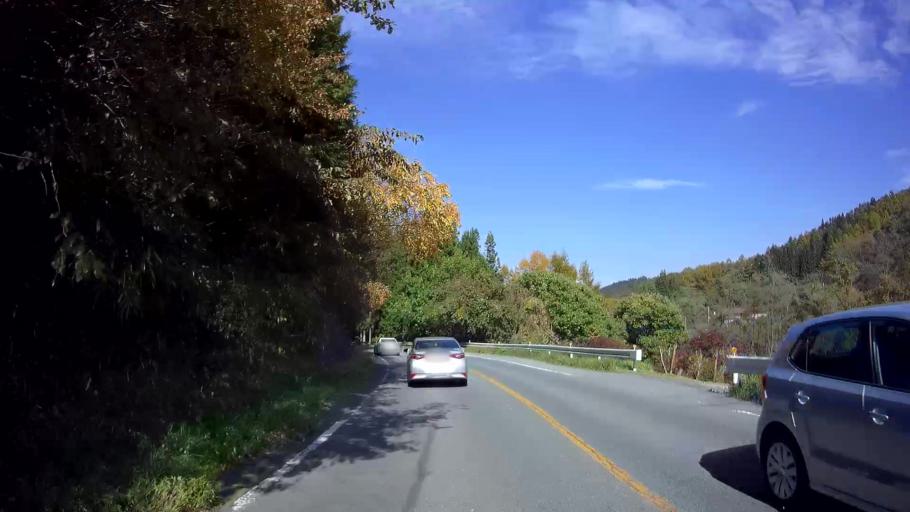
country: JP
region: Gunma
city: Nakanojomachi
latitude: 36.4991
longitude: 138.7770
